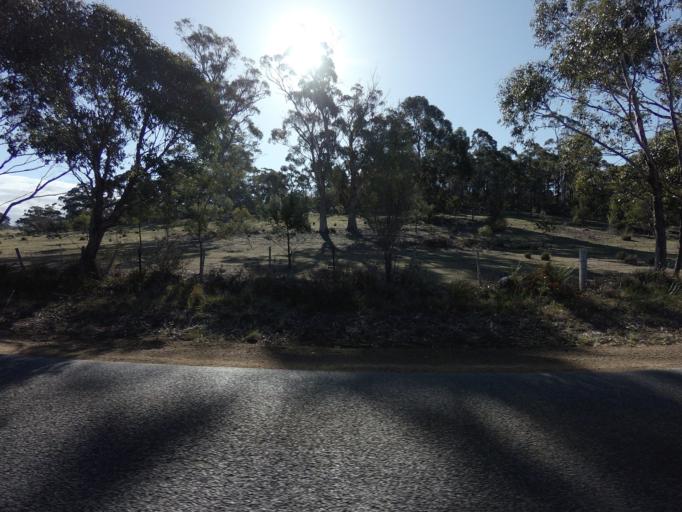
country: AU
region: Tasmania
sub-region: Sorell
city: Sorell
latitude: -42.3162
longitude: 147.9596
